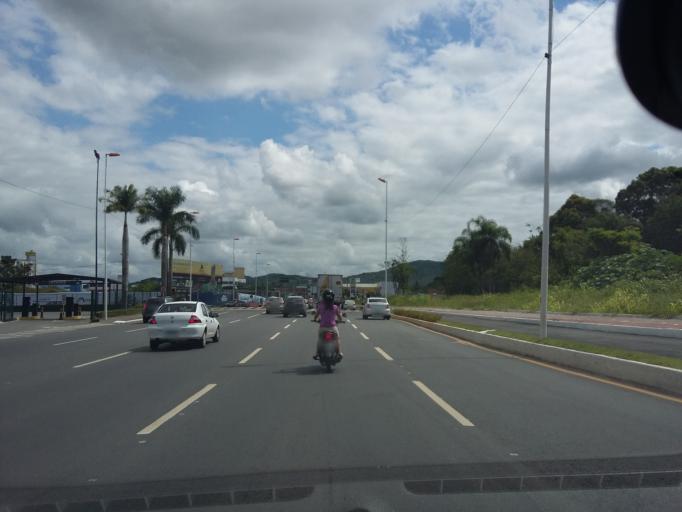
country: BR
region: Santa Catarina
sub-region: Balneario Camboriu
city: Balneario Camboriu
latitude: -26.9926
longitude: -48.6486
